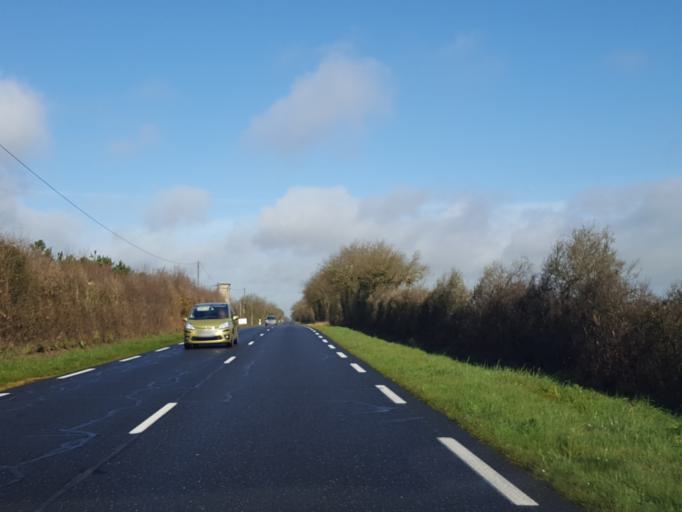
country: FR
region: Pays de la Loire
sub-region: Departement de la Vendee
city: Saligny
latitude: 46.8131
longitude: -1.4623
